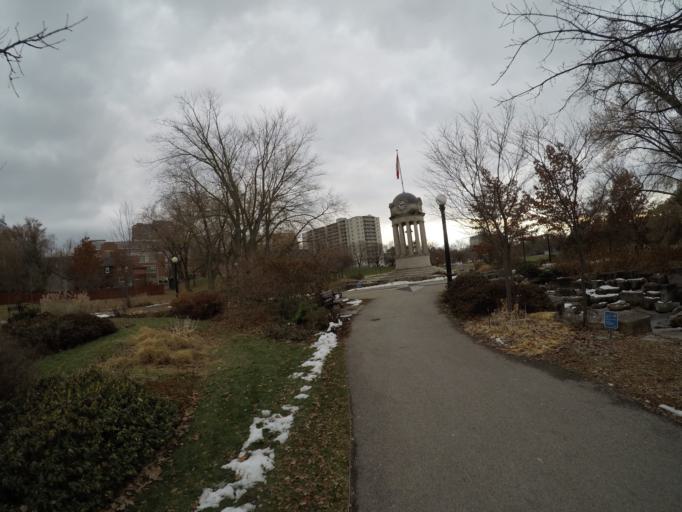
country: CA
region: Ontario
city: Waterloo
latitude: 43.4489
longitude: -80.4938
